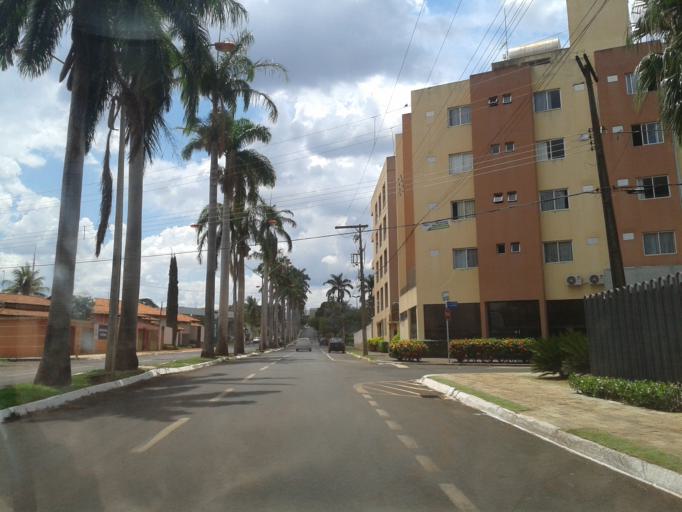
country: BR
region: Goias
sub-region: Itumbiara
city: Itumbiara
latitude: -18.4126
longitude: -49.2099
